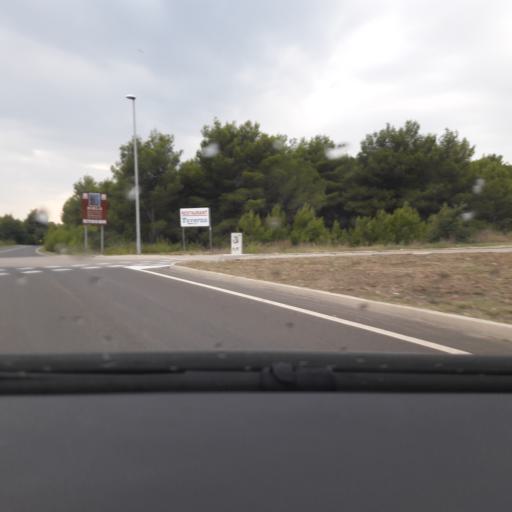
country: HR
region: Zadarska
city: Zadar
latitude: 44.1538
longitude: 15.2158
